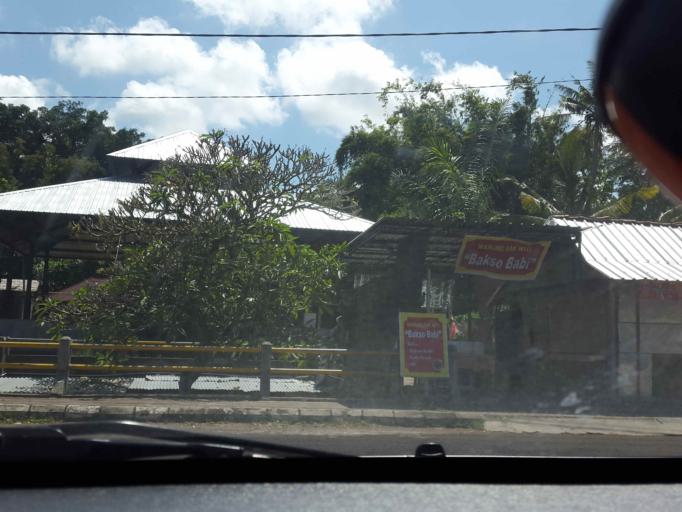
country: ID
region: Bali
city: Klungkung
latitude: -8.5245
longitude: 115.3976
